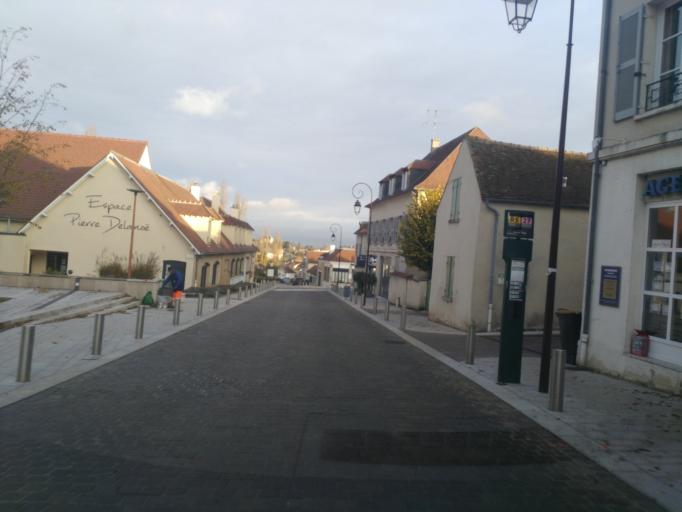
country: FR
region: Ile-de-France
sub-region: Departement des Yvelines
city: Fourqueux
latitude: 48.8866
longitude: 2.0634
